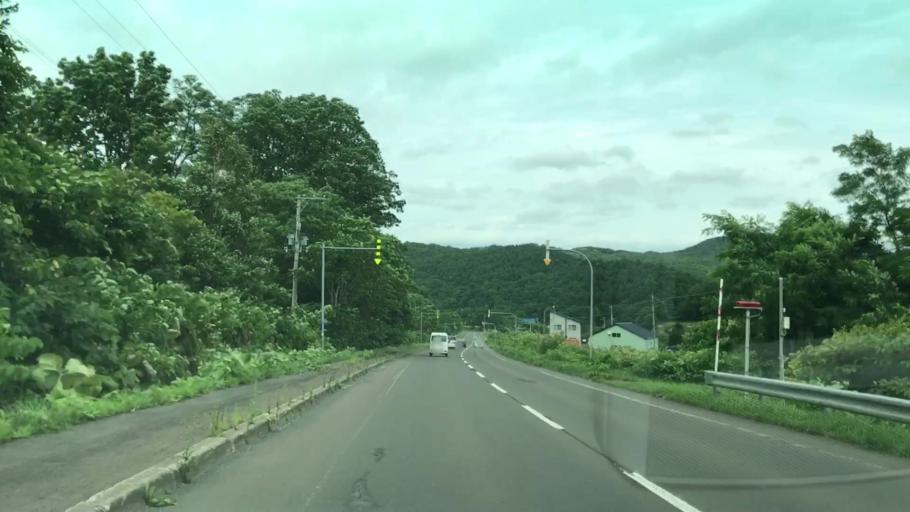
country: JP
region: Hokkaido
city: Niseko Town
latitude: 42.9600
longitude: 140.6941
